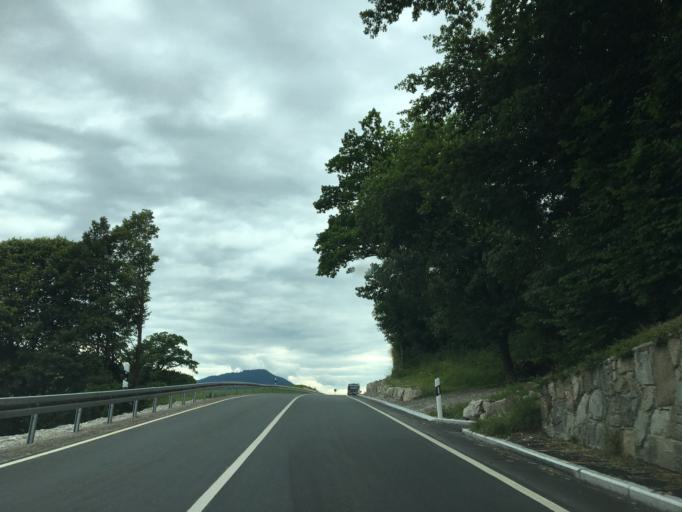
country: DE
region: Bavaria
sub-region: Upper Bavaria
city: Fischbachau
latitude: 47.7633
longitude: 11.9605
